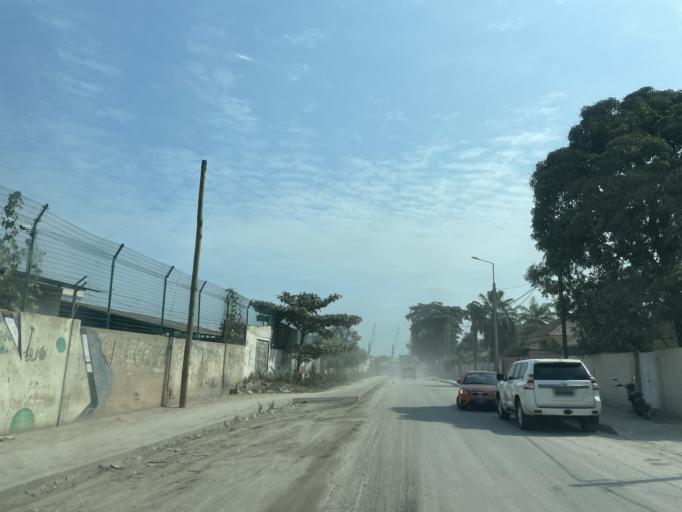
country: AO
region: Luanda
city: Luanda
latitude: -8.8074
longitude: 13.2429
